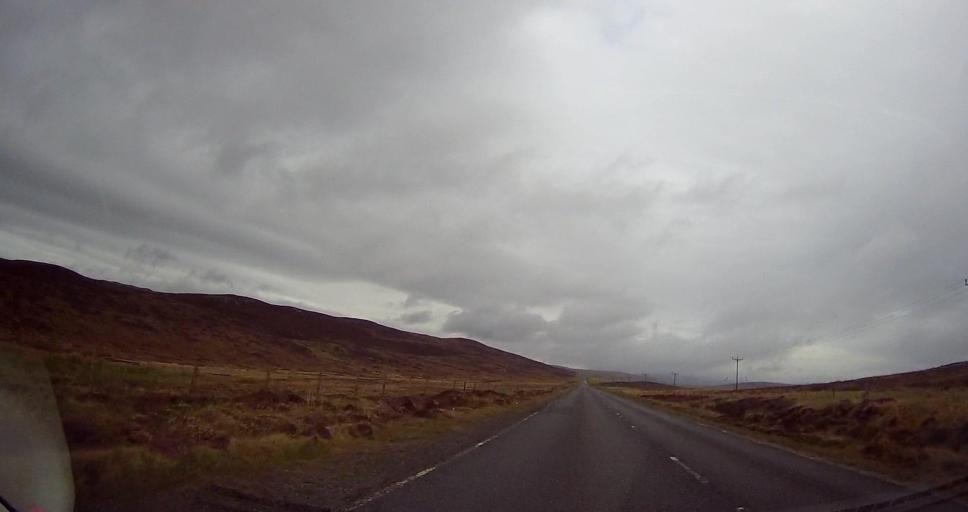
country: GB
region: Scotland
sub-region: Shetland Islands
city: Lerwick
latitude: 60.2055
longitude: -1.2332
